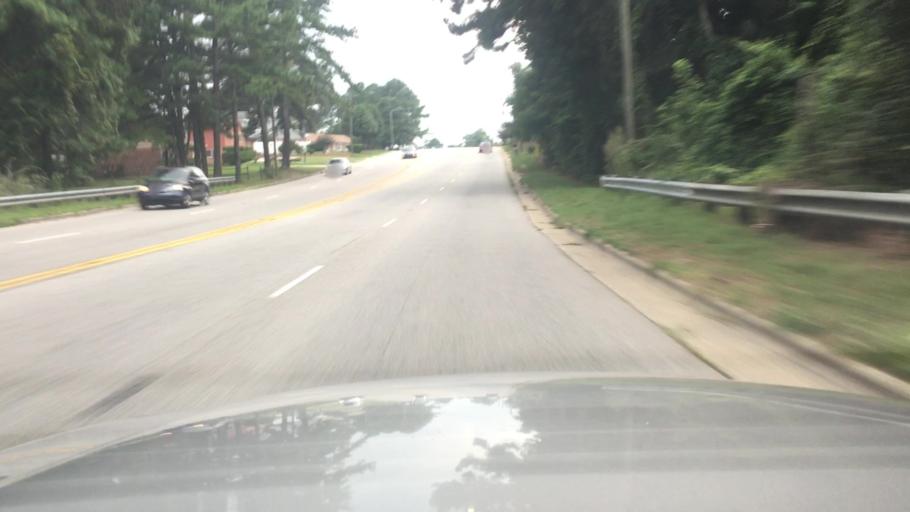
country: US
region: North Carolina
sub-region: Cumberland County
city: Fort Bragg
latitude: 35.0944
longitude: -78.9747
